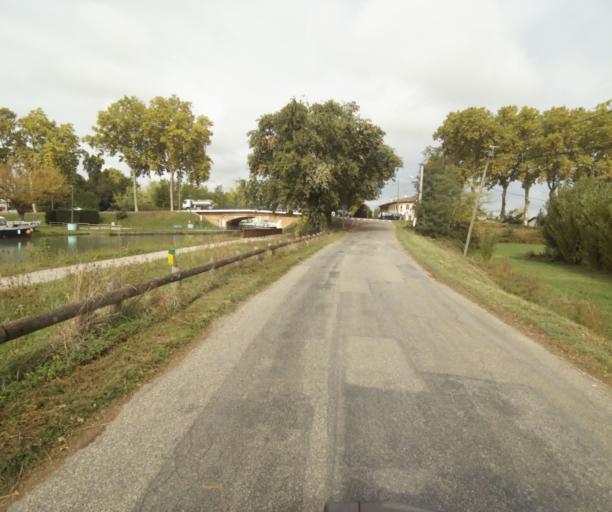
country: FR
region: Midi-Pyrenees
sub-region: Departement du Tarn-et-Garonne
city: Montech
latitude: 43.9591
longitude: 1.2382
